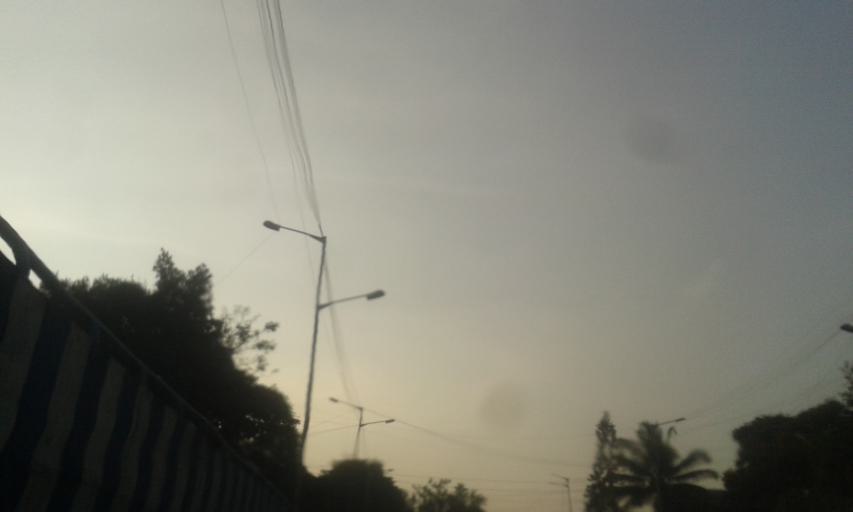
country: IN
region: Karnataka
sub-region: Bangalore Urban
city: Bangalore
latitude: 12.9063
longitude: 77.5836
